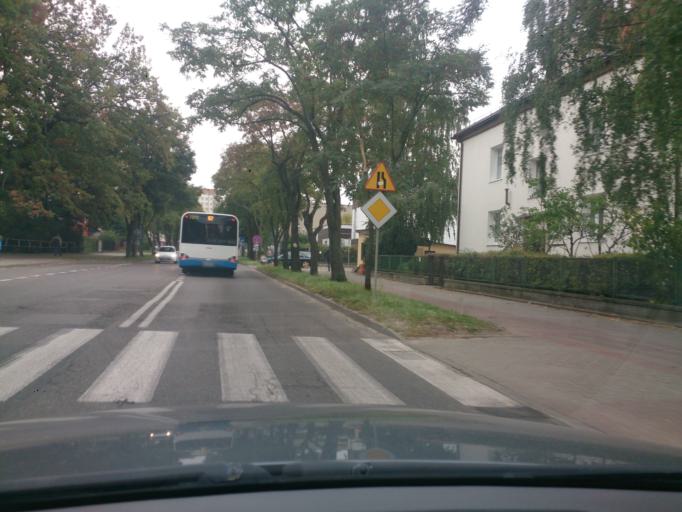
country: PL
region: Pomeranian Voivodeship
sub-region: Powiat wejherowski
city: Rumia
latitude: 54.5716
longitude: 18.3926
